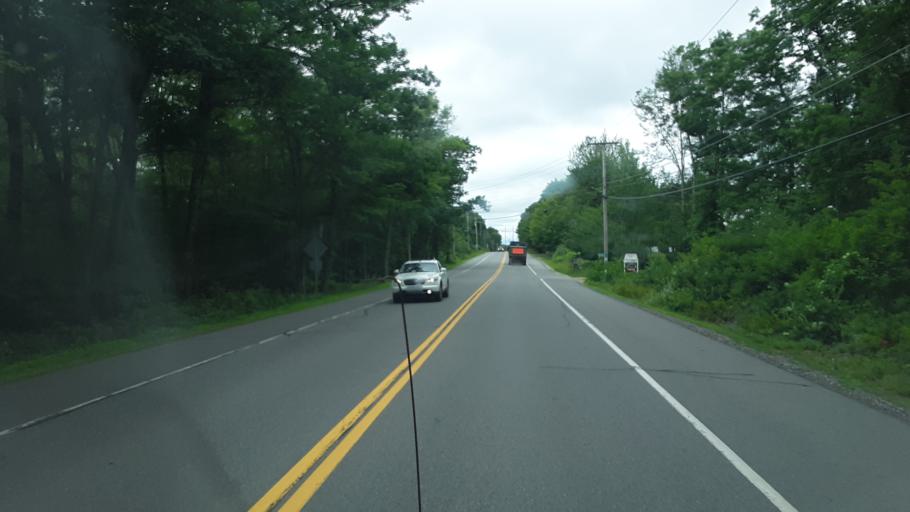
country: US
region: New Hampshire
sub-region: Strafford County
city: Lee
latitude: 43.1535
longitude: -71.0479
